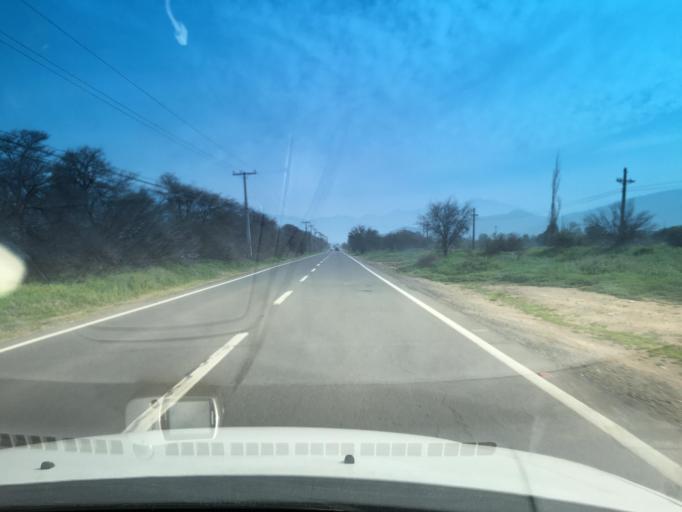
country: CL
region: Santiago Metropolitan
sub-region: Provincia de Chacabuco
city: Lampa
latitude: -33.1597
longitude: -70.8968
